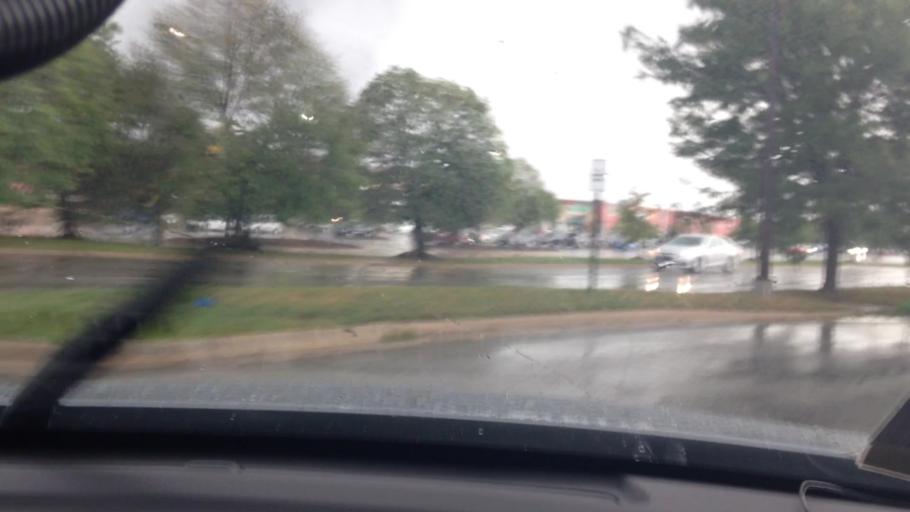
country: US
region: Kansas
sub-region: Johnson County
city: Overland Park
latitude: 38.9174
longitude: -94.6655
